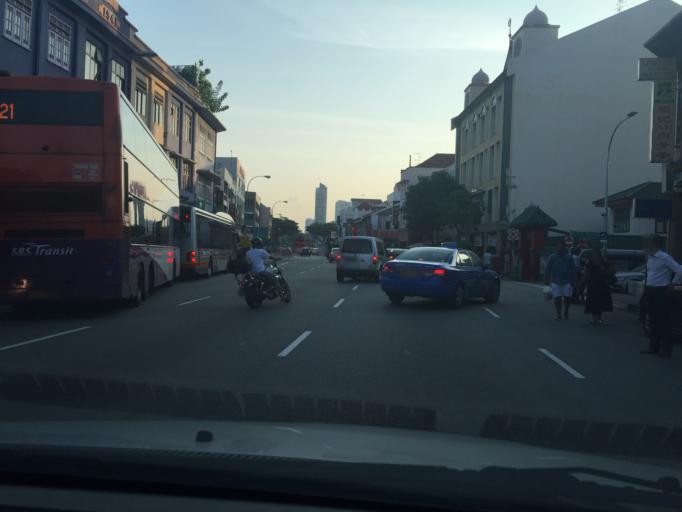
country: SG
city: Singapore
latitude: 1.3123
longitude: 103.8774
